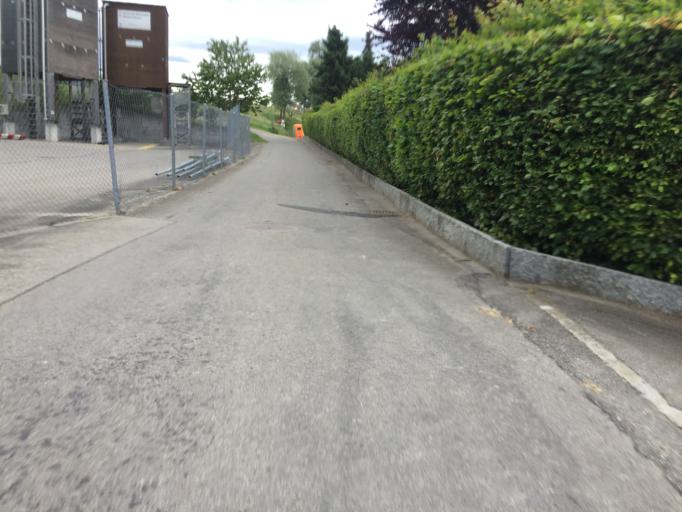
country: CH
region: Bern
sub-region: Bern-Mittelland District
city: Munsingen
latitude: 46.8686
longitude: 7.5669
